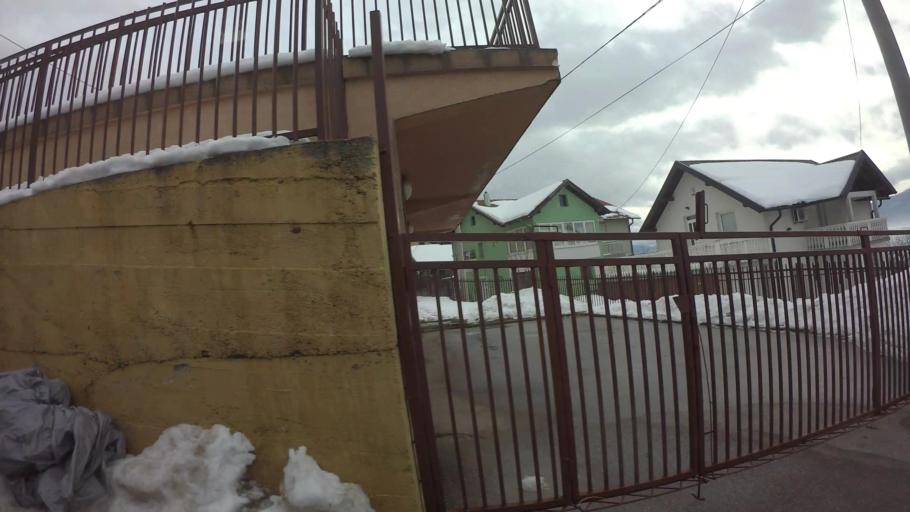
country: BA
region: Federation of Bosnia and Herzegovina
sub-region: Kanton Sarajevo
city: Sarajevo
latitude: 43.8623
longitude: 18.3330
